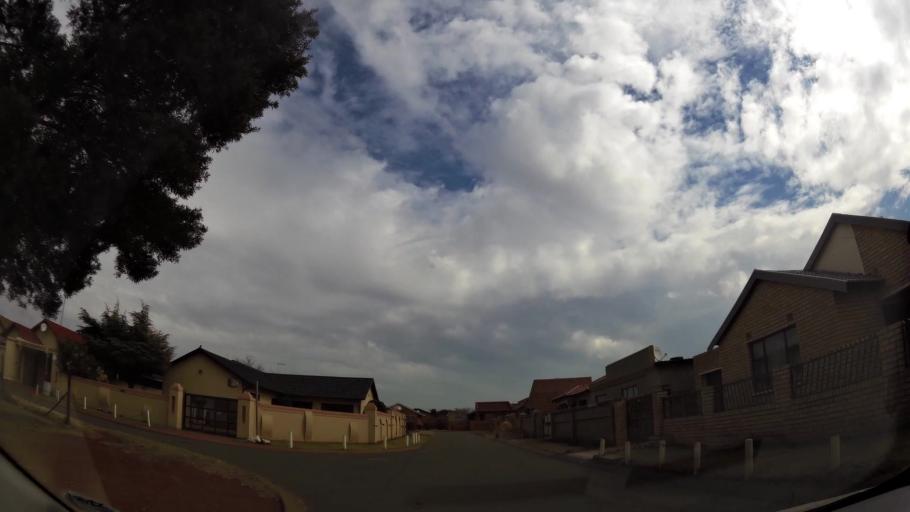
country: ZA
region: Gauteng
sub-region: Ekurhuleni Metropolitan Municipality
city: Germiston
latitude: -26.3743
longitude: 28.1563
